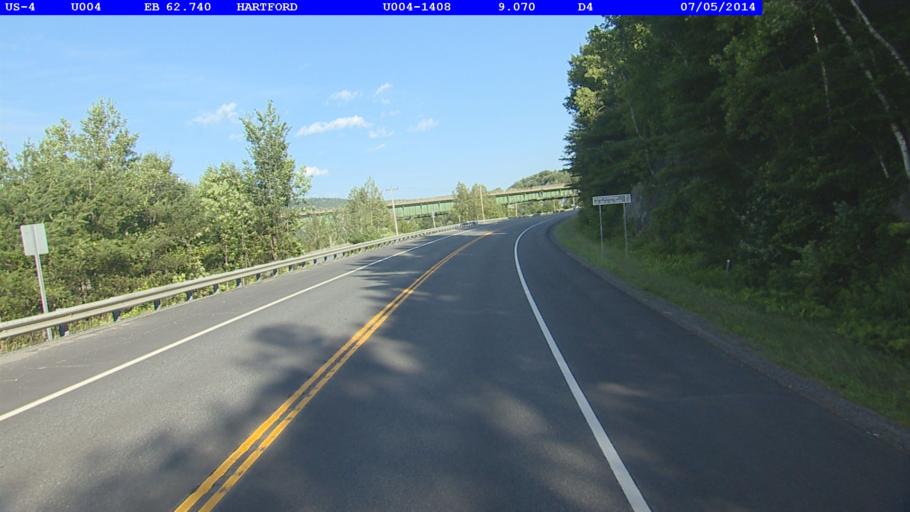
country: US
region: Vermont
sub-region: Windsor County
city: White River Junction
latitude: 43.6550
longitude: -72.3333
